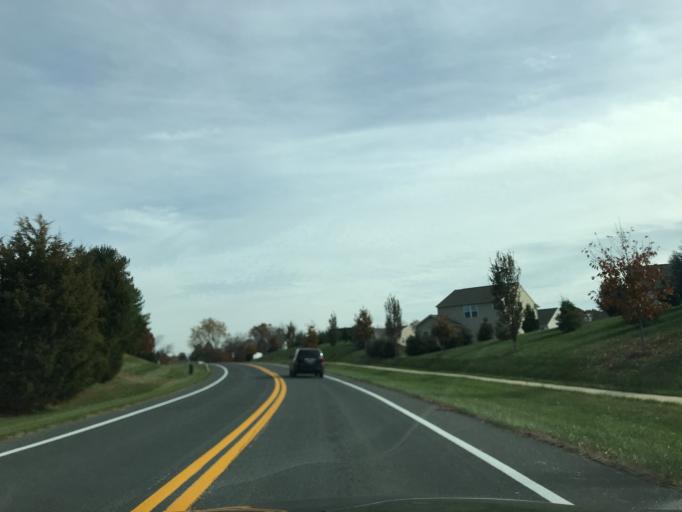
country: US
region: Maryland
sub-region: Carroll County
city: Eldersburg
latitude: 39.4008
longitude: -76.9565
